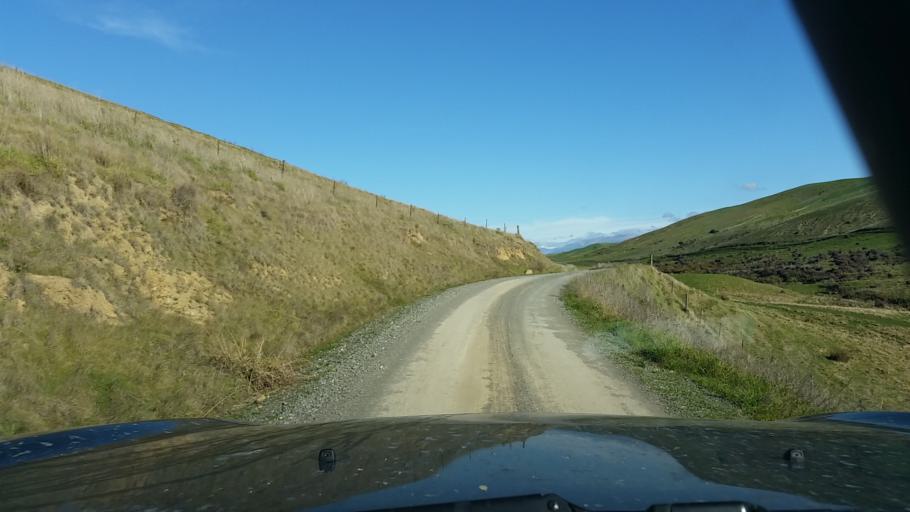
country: NZ
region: Marlborough
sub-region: Marlborough District
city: Blenheim
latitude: -41.6683
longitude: 174.1374
